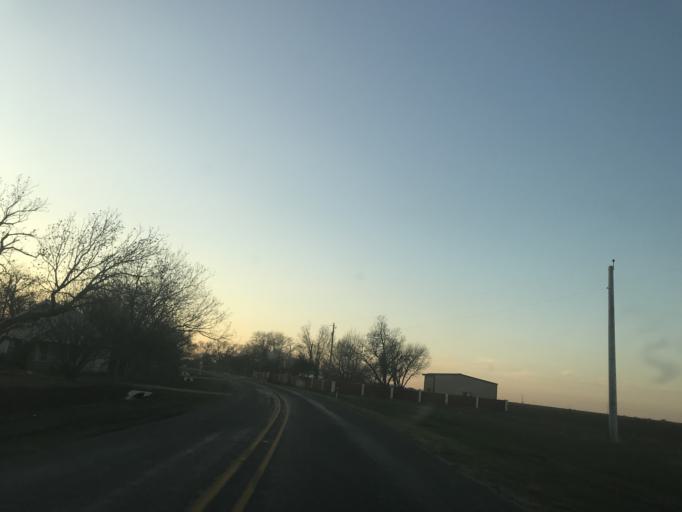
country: US
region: Texas
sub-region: Williamson County
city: Hutto
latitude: 30.4995
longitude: -97.5068
